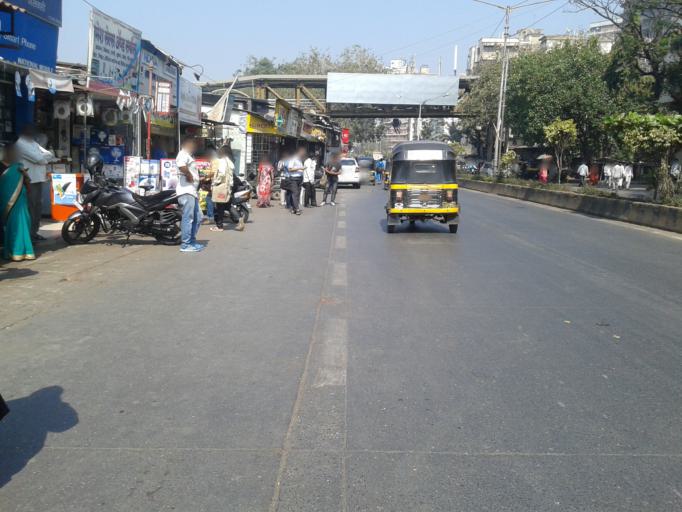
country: IN
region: Maharashtra
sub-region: Mumbai Suburban
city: Borivli
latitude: 19.2485
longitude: 72.8625
